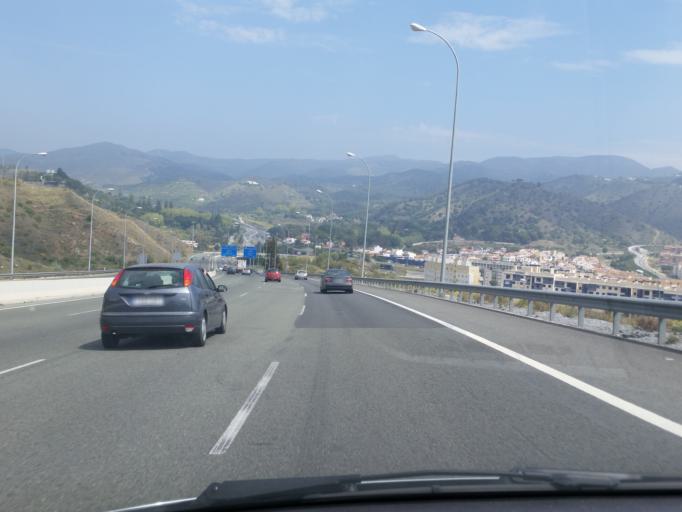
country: ES
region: Andalusia
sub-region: Provincia de Malaga
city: Malaga
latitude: 36.7496
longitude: -4.4324
